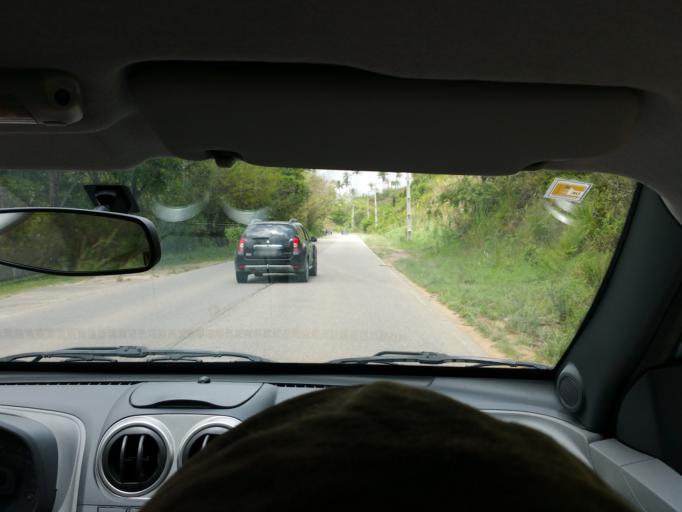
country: BR
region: Pernambuco
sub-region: Sirinhaem
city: Sirinhaem
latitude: -8.6300
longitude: -35.1210
